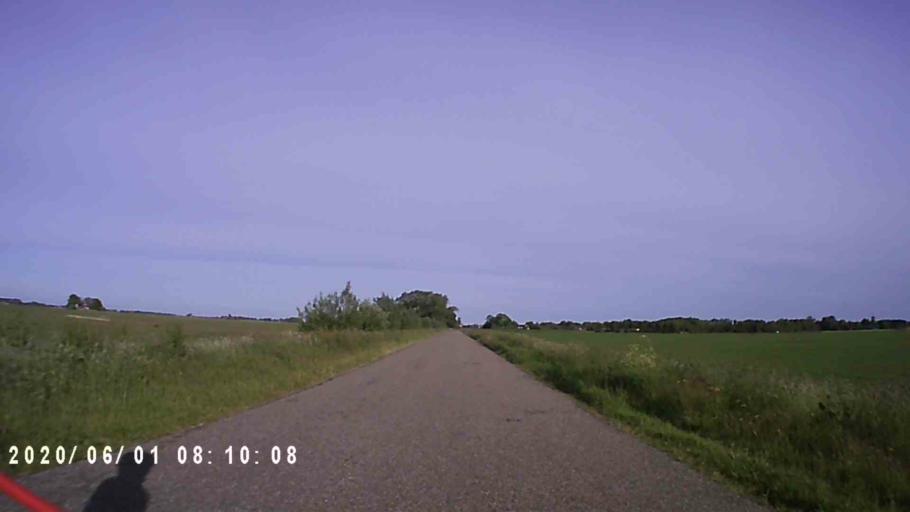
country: NL
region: Friesland
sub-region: Gemeente Ferwerderadiel
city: Burdaard
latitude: 53.2861
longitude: 5.8896
